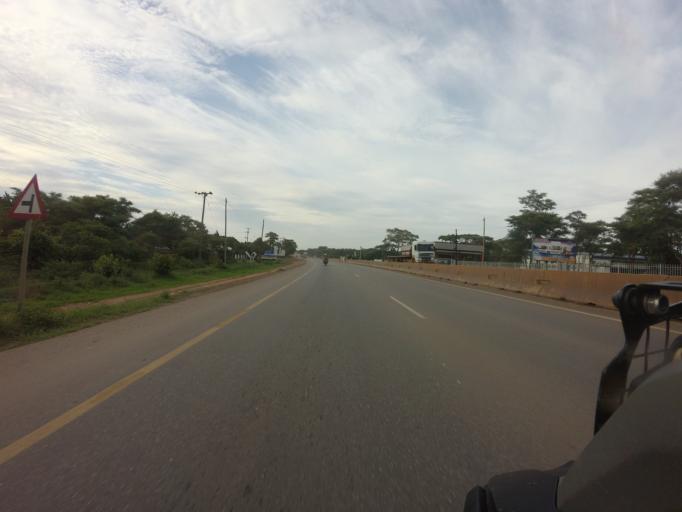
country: ZM
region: Lusaka
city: Lusaka
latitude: -15.5123
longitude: 28.2625
